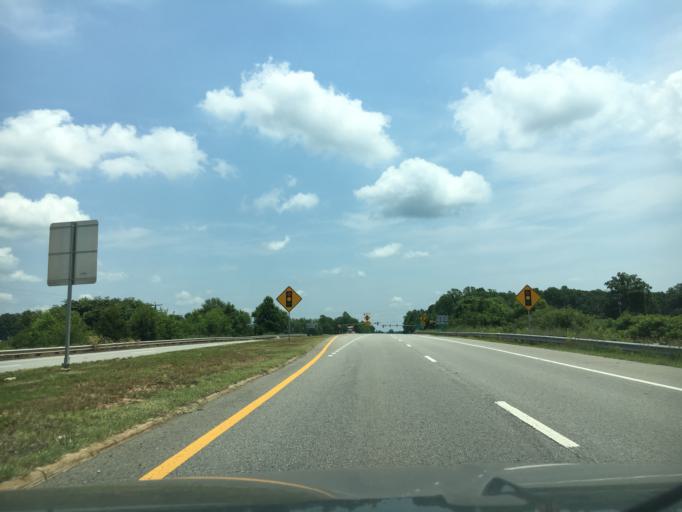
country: US
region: Virginia
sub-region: Buckingham County
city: Buckingham
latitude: 37.5305
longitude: -78.4952
